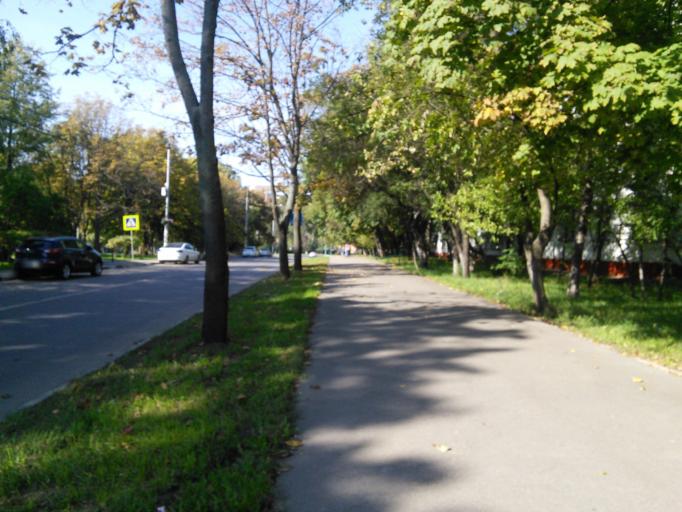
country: RU
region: Moscow
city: Orekhovo-Borisovo Severnoye
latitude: 55.6316
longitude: 37.6703
